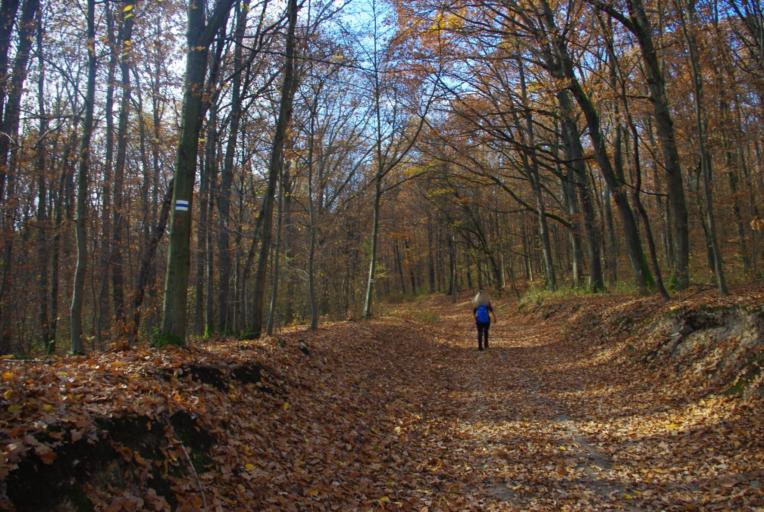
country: HU
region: Borsod-Abauj-Zemplen
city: Sarospatak
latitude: 48.3819
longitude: 21.5438
